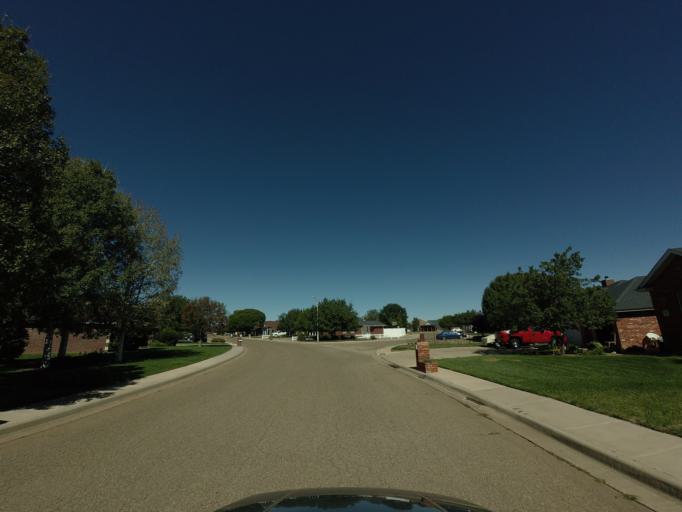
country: US
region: New Mexico
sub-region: Curry County
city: Clovis
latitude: 34.4240
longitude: -103.1703
